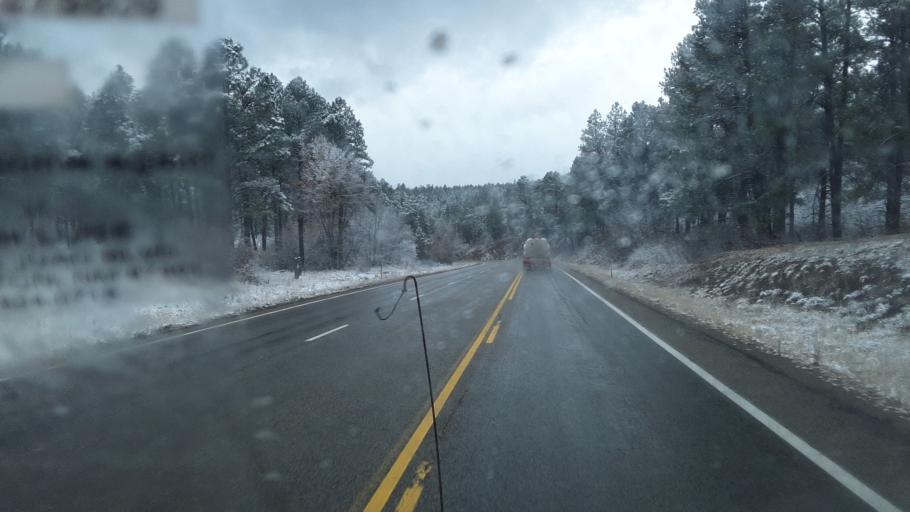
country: US
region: Colorado
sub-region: Archuleta County
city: Pagosa Springs
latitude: 37.2131
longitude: -107.2901
